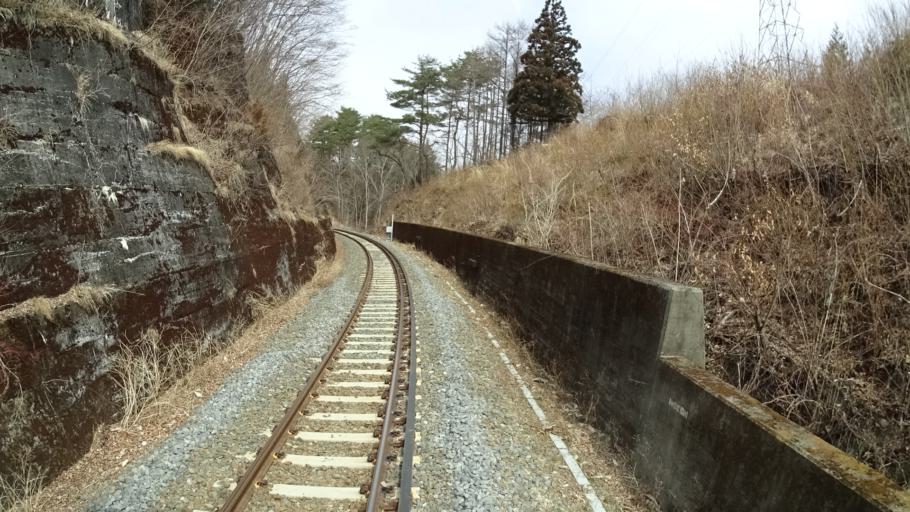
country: JP
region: Iwate
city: Yamada
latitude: 39.5000
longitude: 141.9296
